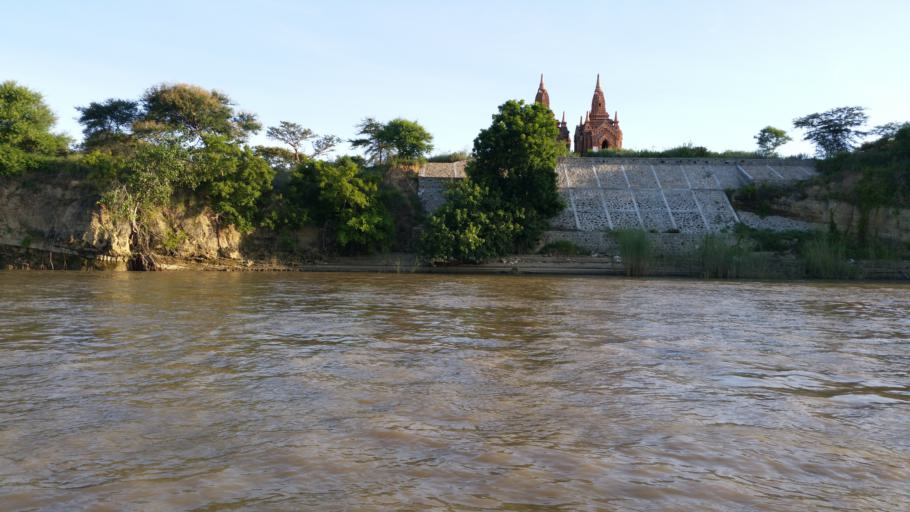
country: MM
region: Magway
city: Pakokku
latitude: 21.1845
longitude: 94.8719
